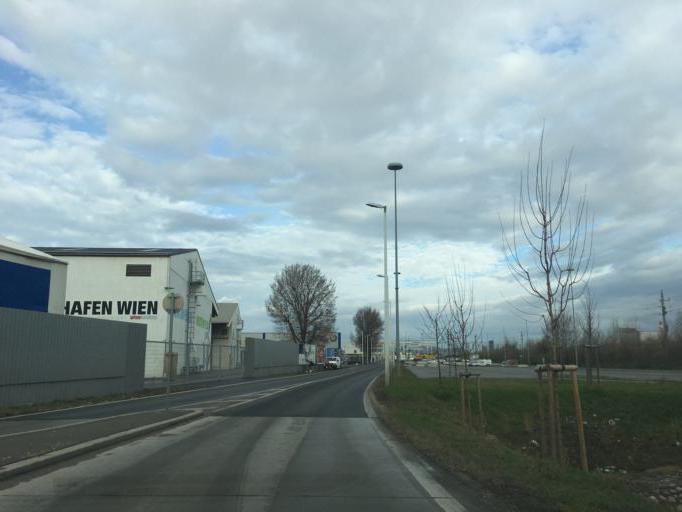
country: AT
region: Lower Austria
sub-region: Politischer Bezirk Wien-Umgebung
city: Schwechat
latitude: 48.1753
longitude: 16.4777
